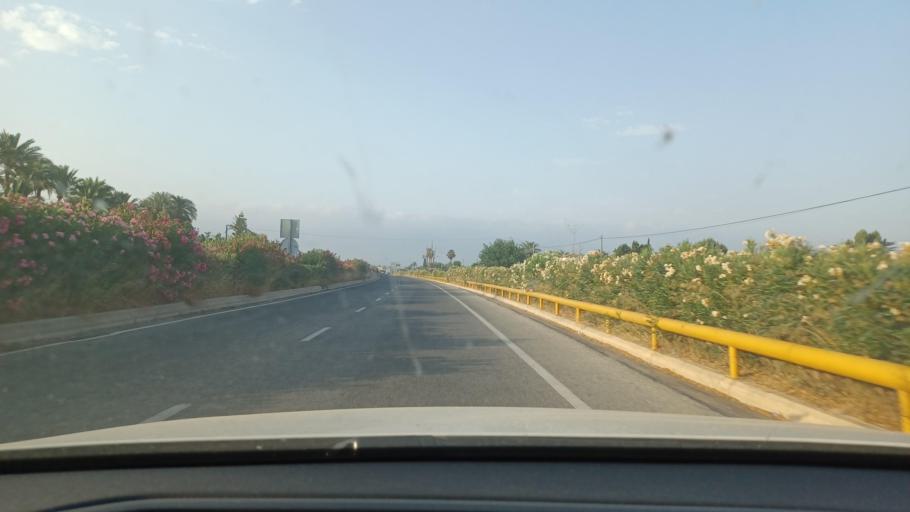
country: ES
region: Valencia
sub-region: Provincia de Alicante
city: Elche
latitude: 38.1937
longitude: -0.7010
